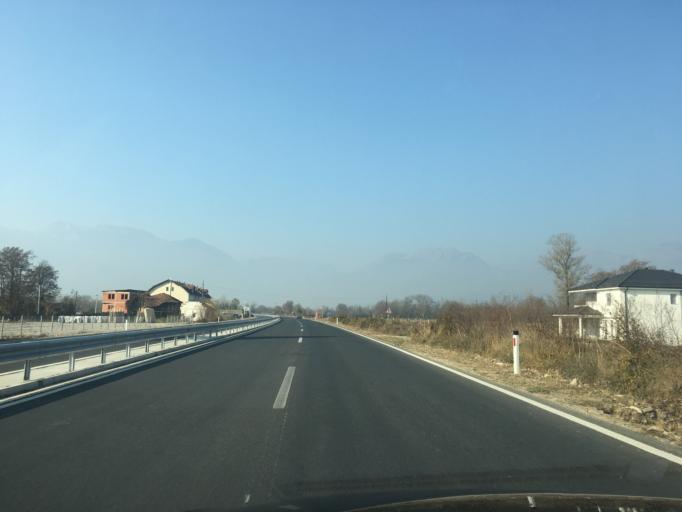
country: XK
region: Pec
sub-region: Komuna e Pejes
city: Dubova (Driloni)
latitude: 42.6595
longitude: 20.3698
